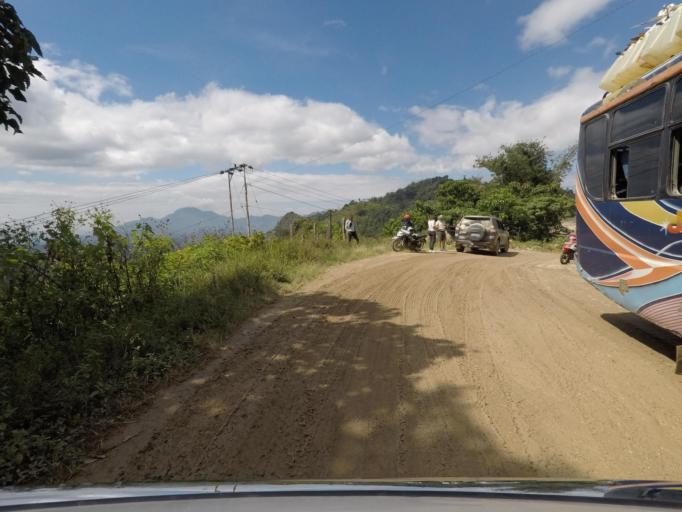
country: TL
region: Baucau
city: Venilale
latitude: -8.7184
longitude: 126.3672
